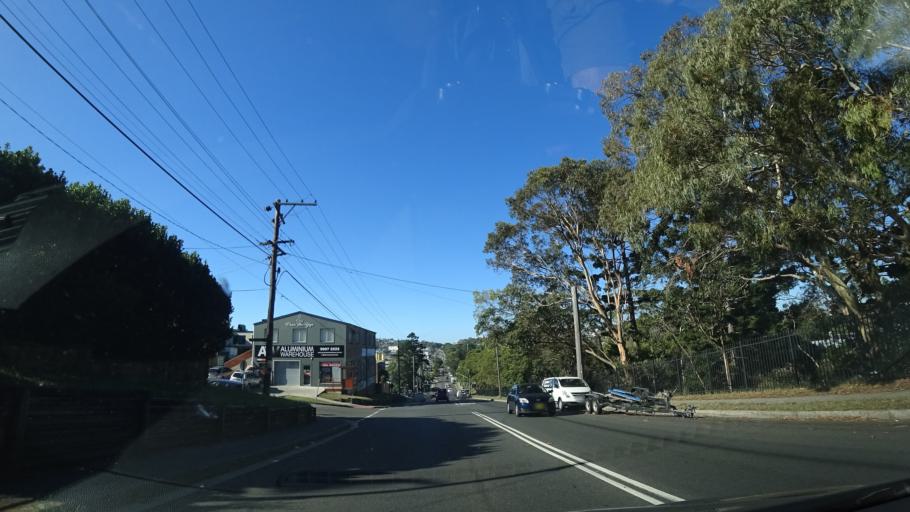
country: AU
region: New South Wales
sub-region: Warringah
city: Brookvale
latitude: -33.7687
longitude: 151.2787
